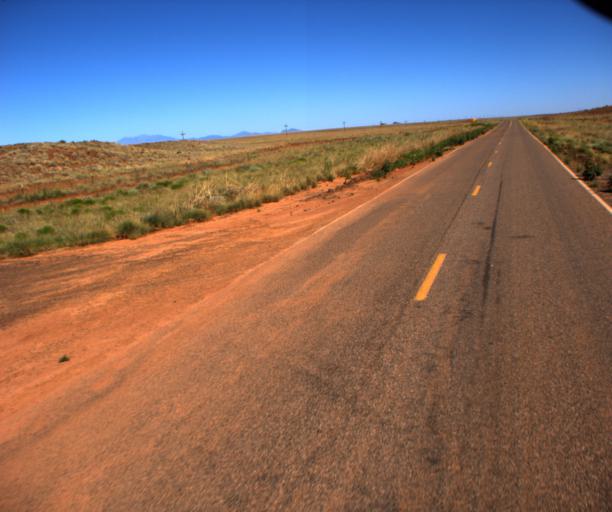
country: US
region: Arizona
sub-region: Coconino County
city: LeChee
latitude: 35.1598
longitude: -110.9083
